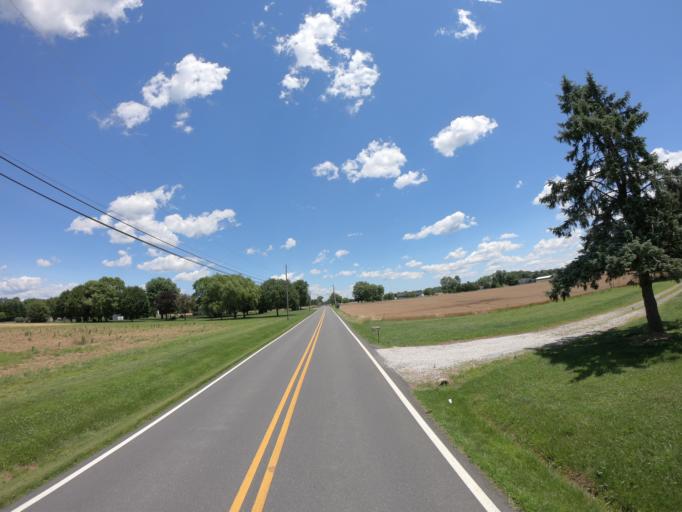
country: US
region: Delaware
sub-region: New Castle County
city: Middletown
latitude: 39.4634
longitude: -75.7611
